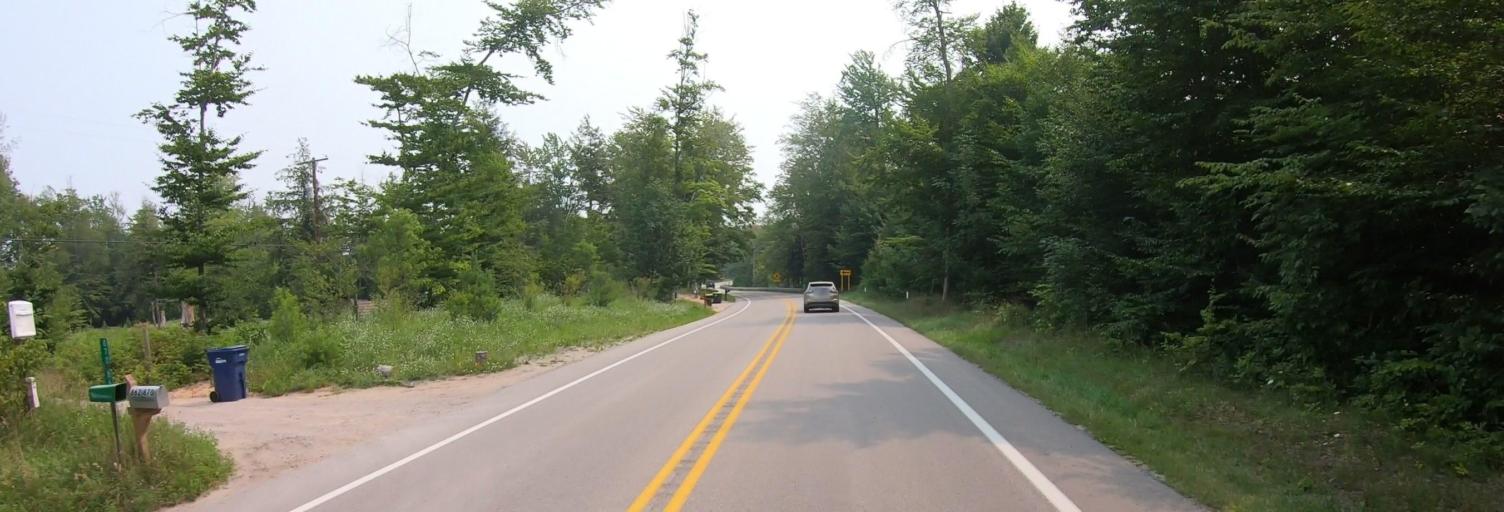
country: US
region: Michigan
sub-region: Leelanau County
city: Leland
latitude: 44.9164
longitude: -85.8346
